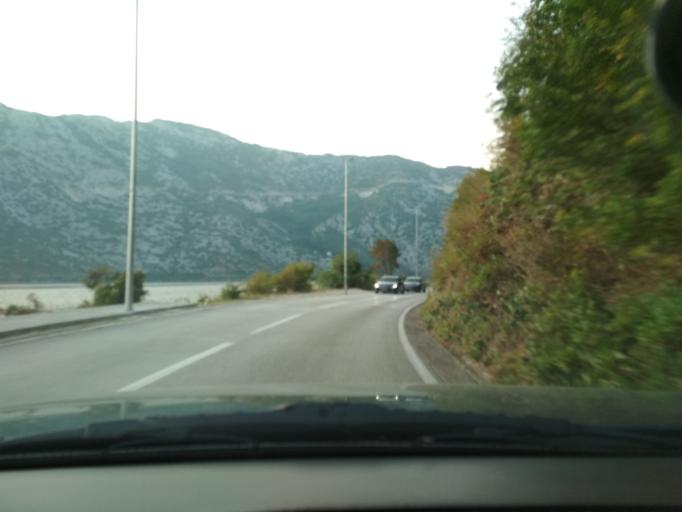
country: ME
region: Kotor
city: Risan
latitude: 42.5010
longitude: 18.6924
